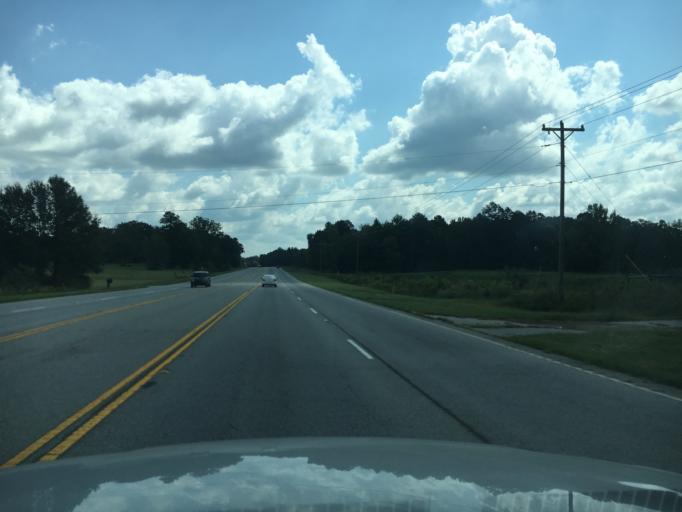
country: US
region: South Carolina
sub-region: Anderson County
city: Williamston
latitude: 34.6154
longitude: -82.3782
